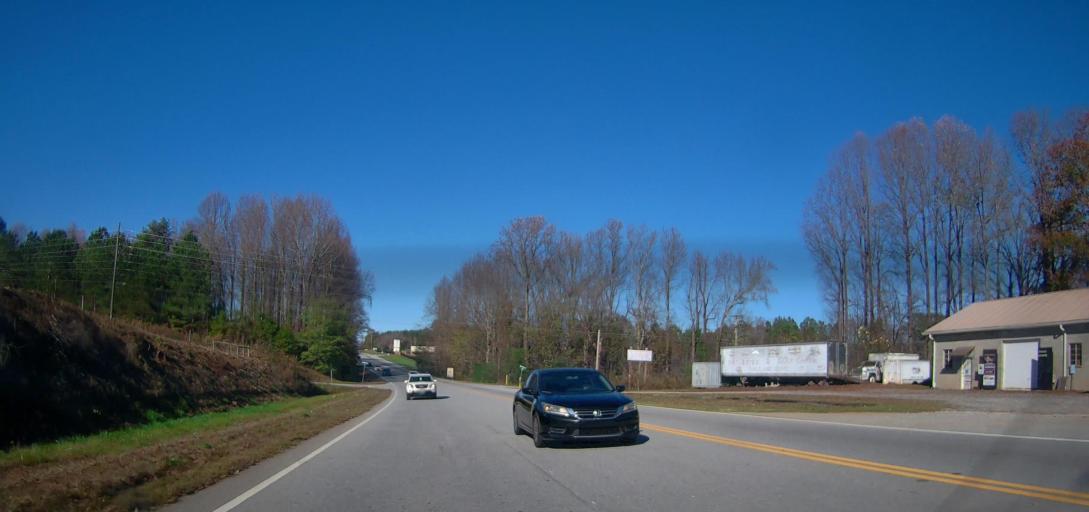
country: US
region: Georgia
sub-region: White County
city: Cleveland
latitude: 34.4952
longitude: -83.7560
